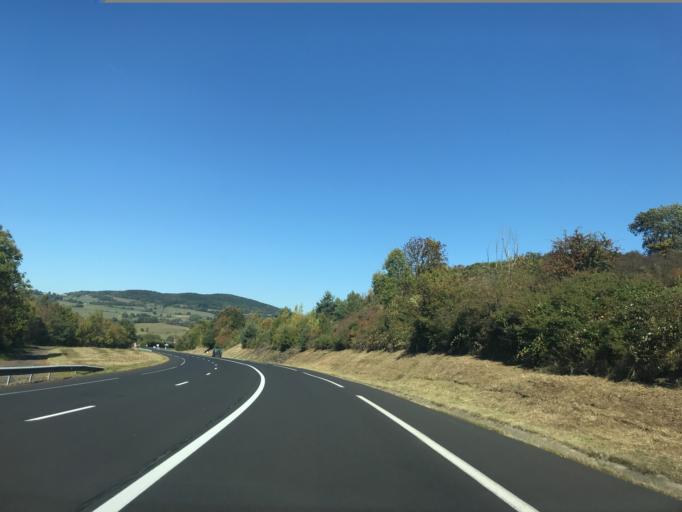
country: FR
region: Auvergne
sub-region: Departement du Puy-de-Dome
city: Gelles
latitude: 45.7182
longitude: 2.8060
